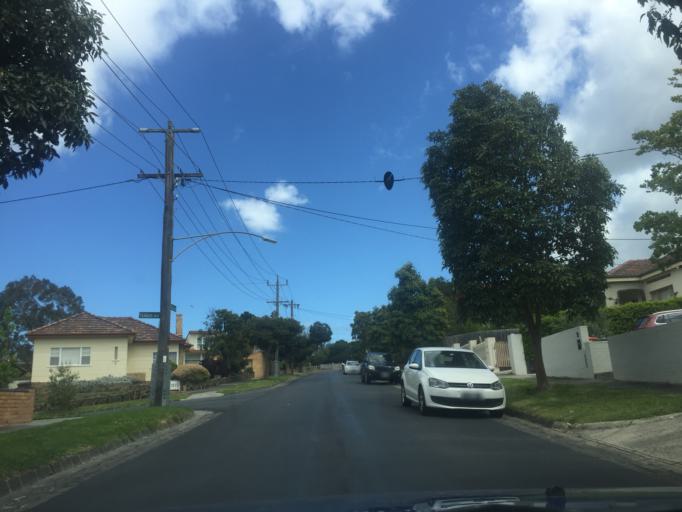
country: AU
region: Victoria
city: Alphington
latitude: -37.7942
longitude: 145.0386
